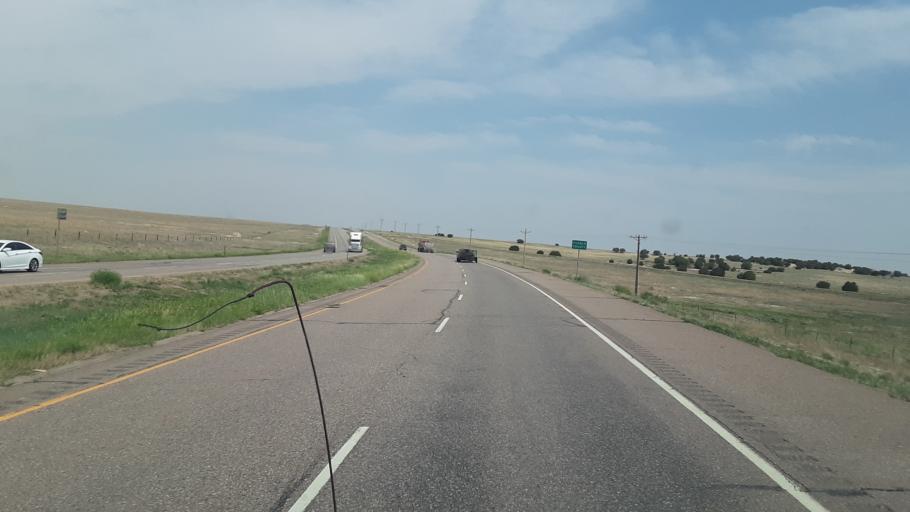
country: US
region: Colorado
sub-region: Fremont County
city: Penrose
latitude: 38.3722
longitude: -104.9416
